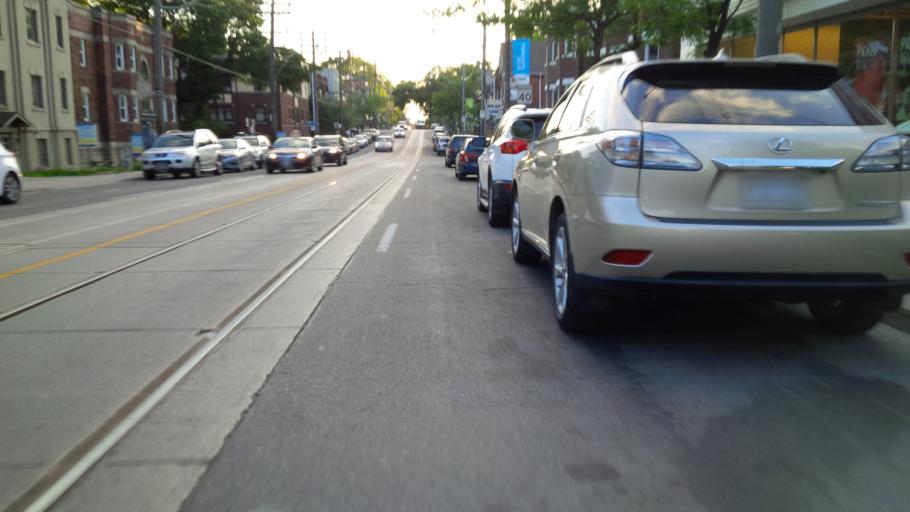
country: CA
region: Ontario
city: Scarborough
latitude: 43.6731
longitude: -79.2856
